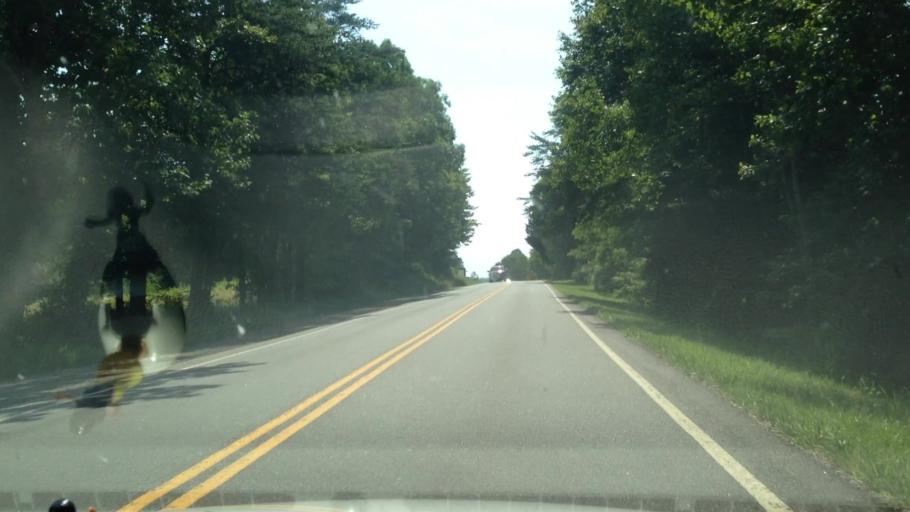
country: US
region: Virginia
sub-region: Patrick County
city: Stuart
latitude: 36.5867
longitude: -80.3952
